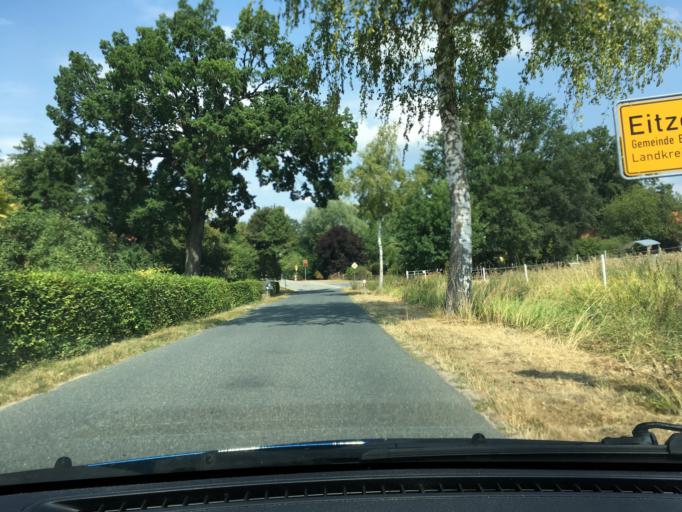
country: DE
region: Lower Saxony
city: Bienenbuttel
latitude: 53.1332
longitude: 10.4325
